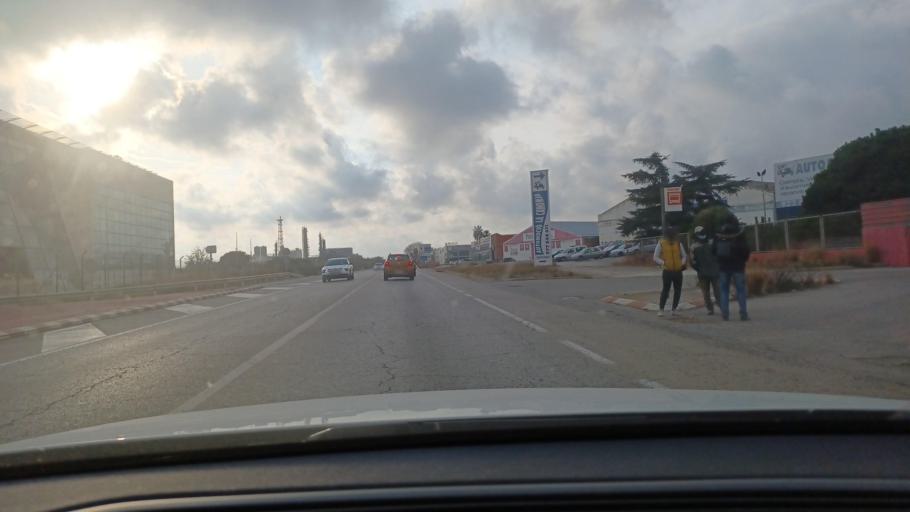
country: ES
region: Catalonia
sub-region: Provincia de Tarragona
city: Vila-seca
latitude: 41.1142
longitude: 1.1743
